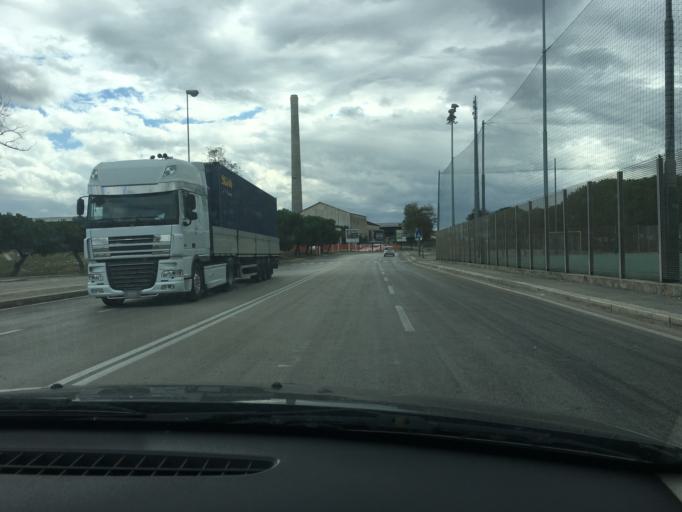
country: IT
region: Apulia
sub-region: Provincia di Bari
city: Bari
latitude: 41.1319
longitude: 16.8410
